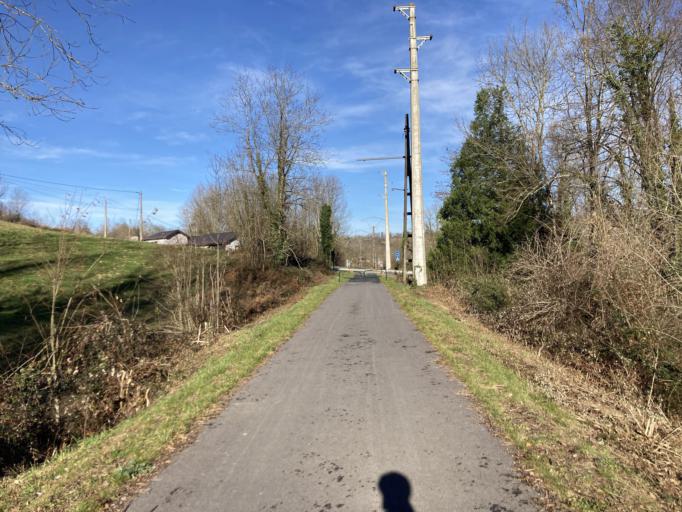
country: FR
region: Aquitaine
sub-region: Departement des Pyrenees-Atlantiques
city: Arudy
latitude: 43.1140
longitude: -0.4378
